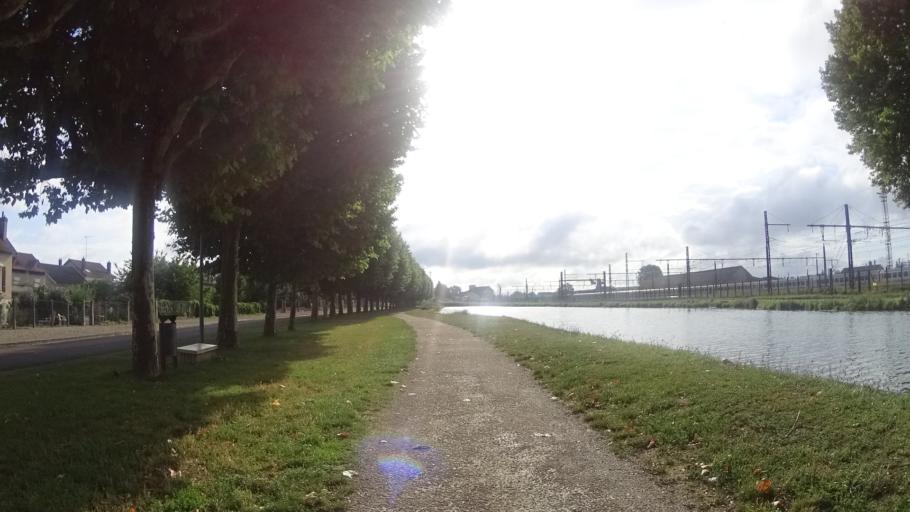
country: FR
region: Bourgogne
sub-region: Departement de l'Yonne
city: Migennes
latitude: 47.9624
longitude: 3.5198
